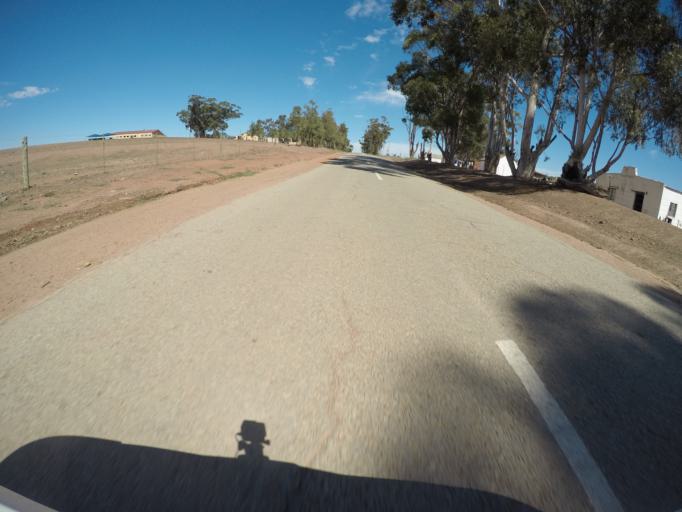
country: ZA
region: Western Cape
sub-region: City of Cape Town
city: Atlantis
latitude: -33.6107
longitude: 18.6373
